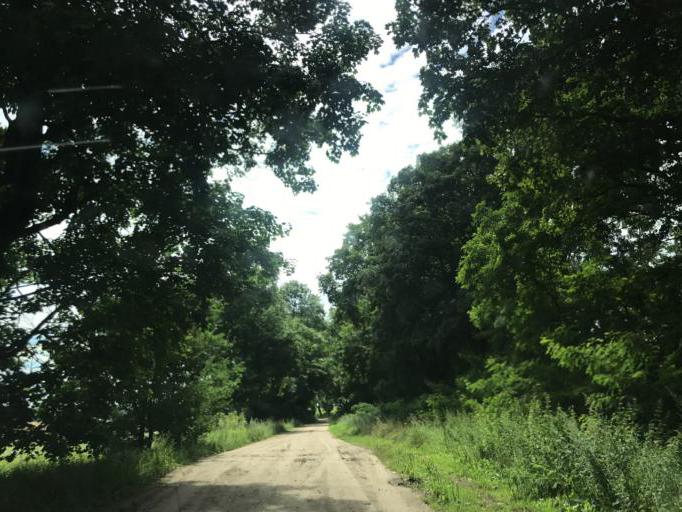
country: DE
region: Mecklenburg-Vorpommern
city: Rechlin
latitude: 53.3348
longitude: 12.7612
